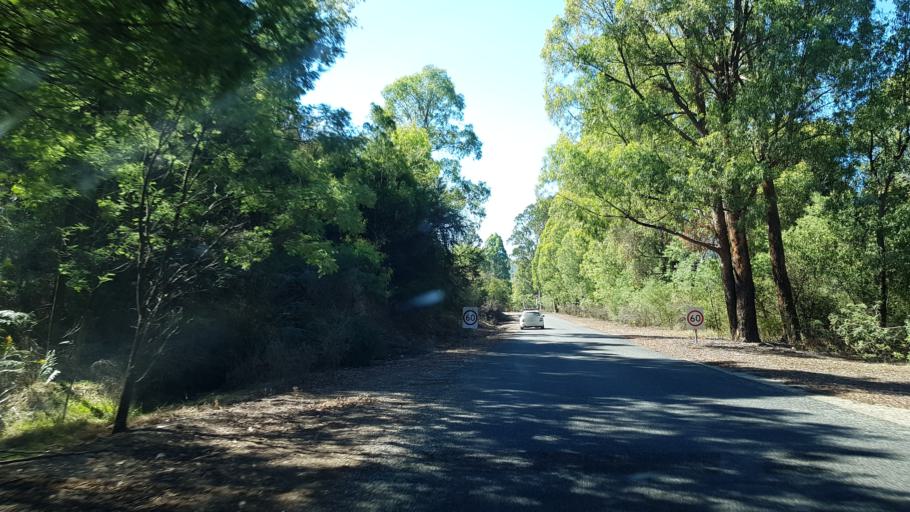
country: AU
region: Victoria
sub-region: Mansfield
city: Mansfield
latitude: -36.9079
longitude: 146.3914
